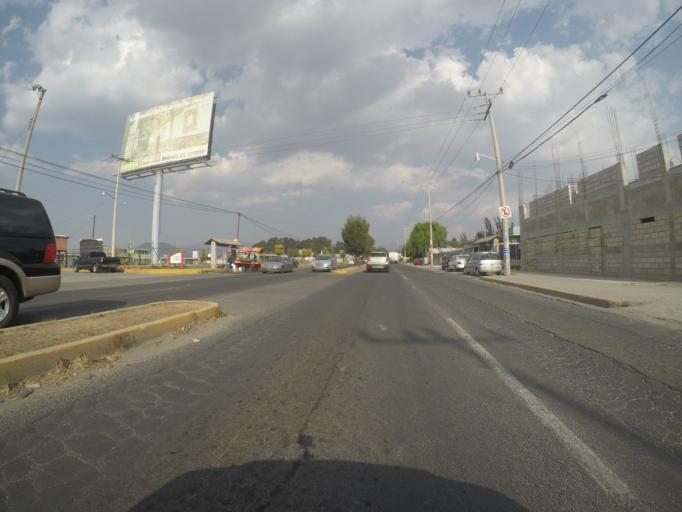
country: MX
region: Mexico
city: Santa Cruz Atizapan
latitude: 19.1839
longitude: -99.4940
